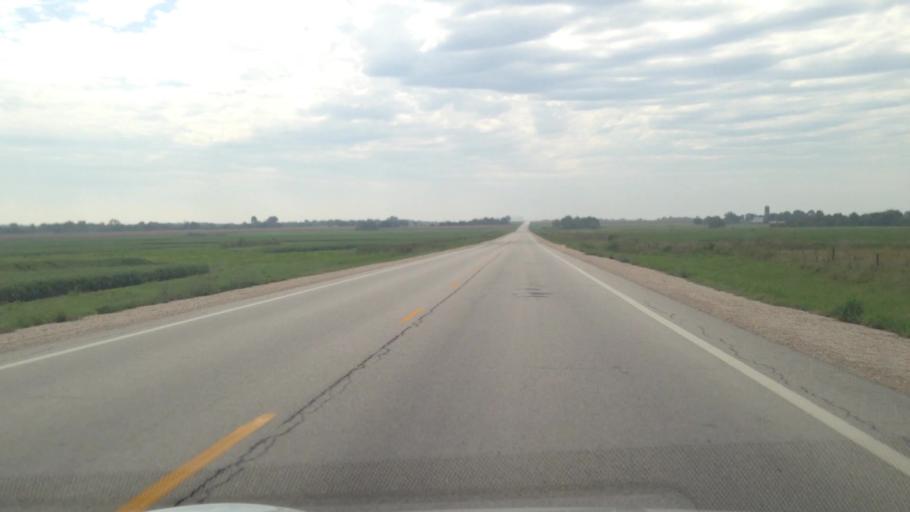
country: US
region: Kansas
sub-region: Anderson County
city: Garnett
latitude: 38.0779
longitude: -95.1694
